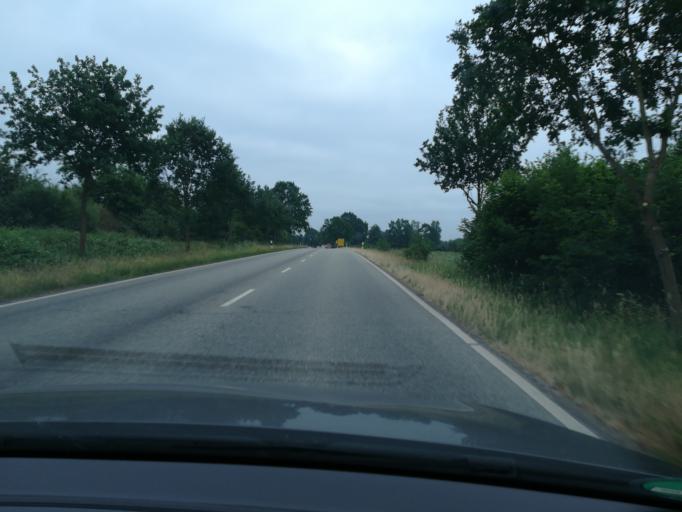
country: DE
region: Schleswig-Holstein
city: Siek
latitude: 53.6365
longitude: 10.3070
